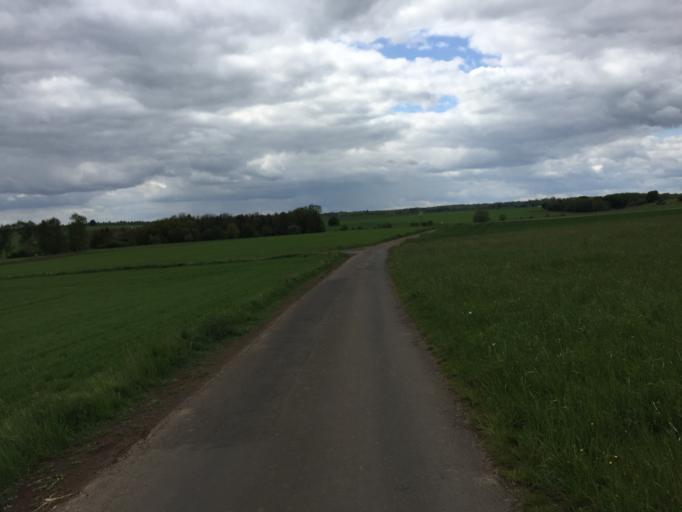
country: DE
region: Hesse
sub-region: Regierungsbezirk Giessen
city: Grunberg
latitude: 50.5712
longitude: 8.8969
